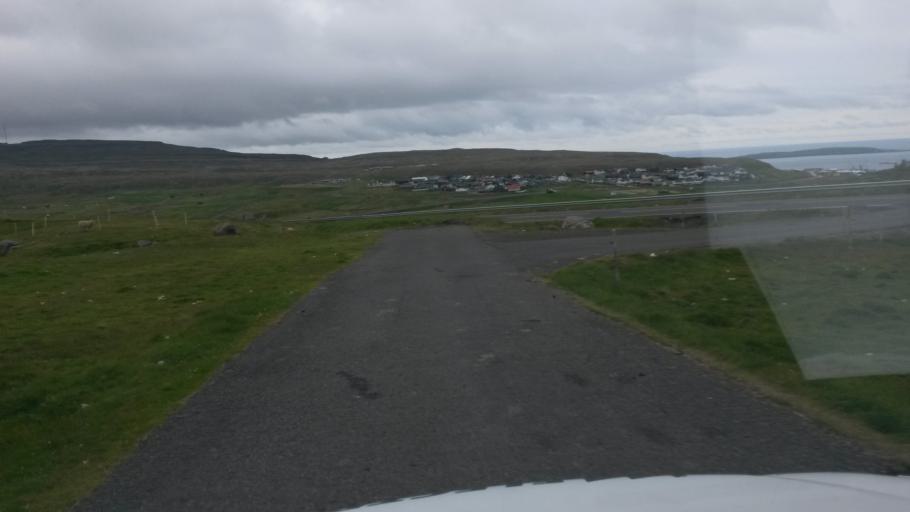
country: FO
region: Streymoy
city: Argir
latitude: 61.9956
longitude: -6.8450
